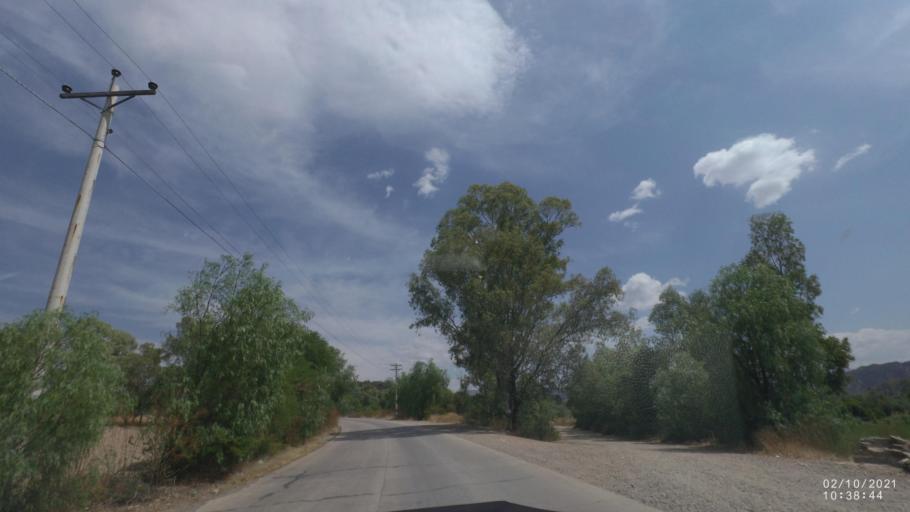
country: BO
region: Cochabamba
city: Capinota
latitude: -17.6317
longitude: -66.2662
